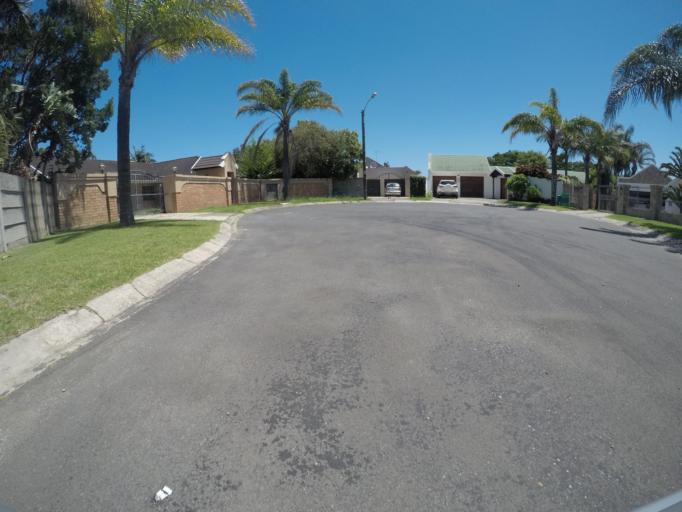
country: ZA
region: Eastern Cape
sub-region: Buffalo City Metropolitan Municipality
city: East London
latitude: -32.9573
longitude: 27.9385
